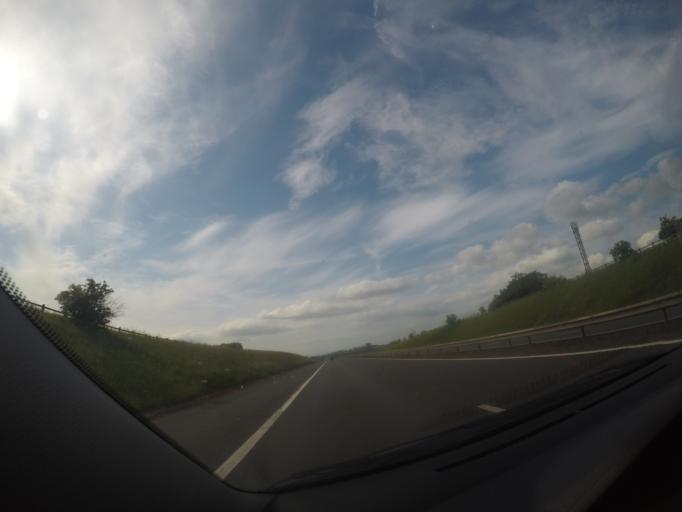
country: GB
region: Scotland
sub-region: South Lanarkshire
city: Lesmahagow
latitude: 55.6128
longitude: -3.8474
